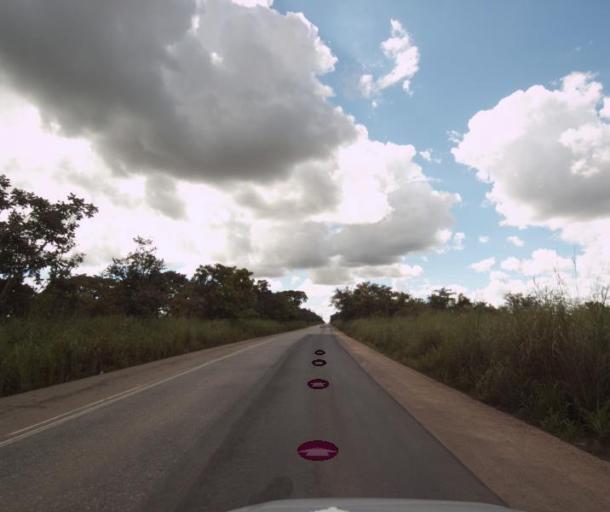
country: BR
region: Goias
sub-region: Porangatu
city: Porangatu
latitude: -13.5482
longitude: -49.1011
